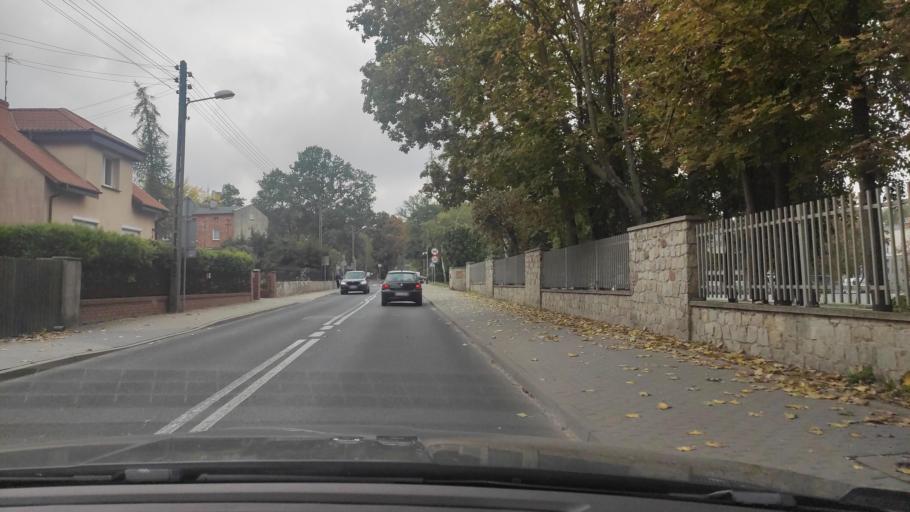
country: PL
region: Greater Poland Voivodeship
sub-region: Powiat poznanski
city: Swarzedz
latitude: 52.4111
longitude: 17.0717
